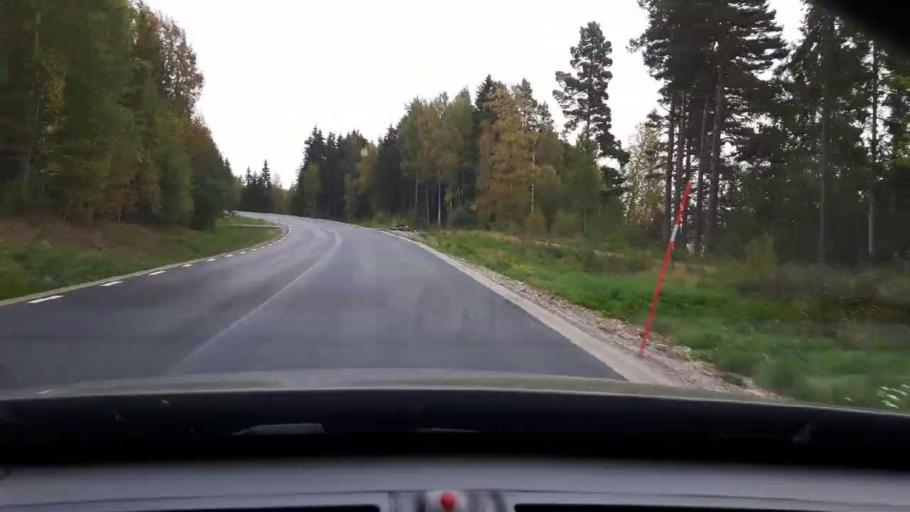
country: SE
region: Dalarna
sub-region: Ludvika Kommun
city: Grangesberg
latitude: 60.2361
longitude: 15.0221
